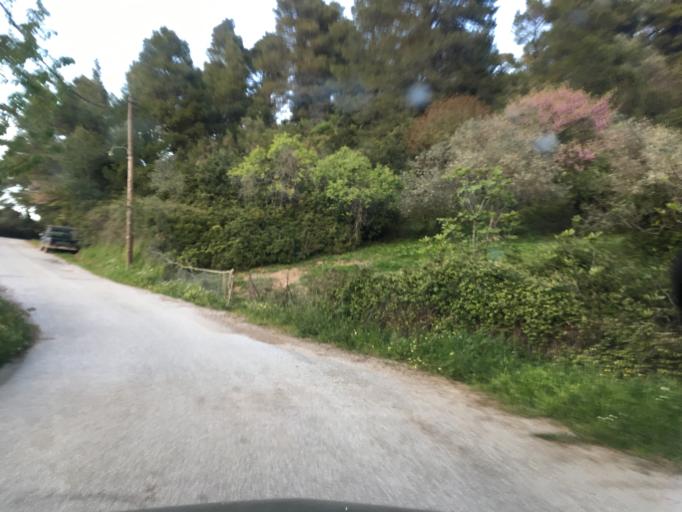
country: GR
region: Thessaly
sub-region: Nomos Magnisias
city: Skiathos
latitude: 39.1860
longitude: 23.6134
